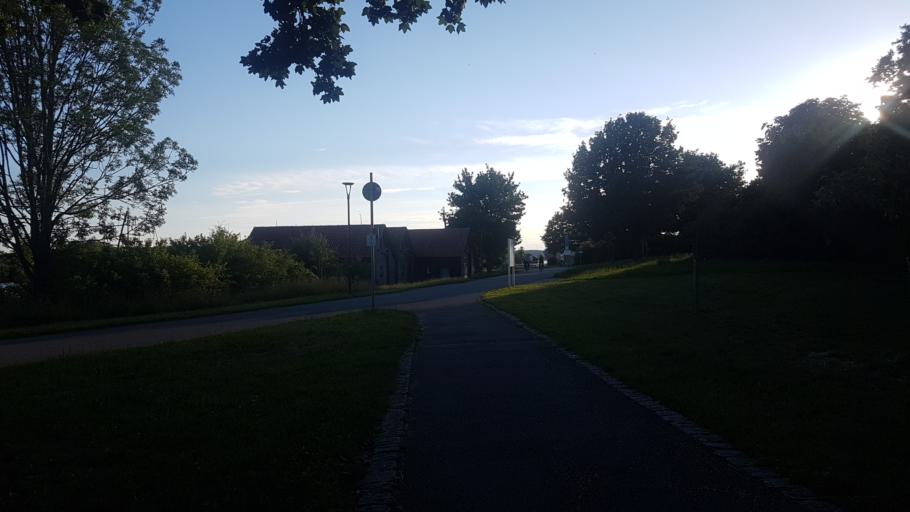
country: DE
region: Bavaria
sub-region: Regierungsbezirk Mittelfranken
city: Gunzenhausen
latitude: 49.1248
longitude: 10.7408
